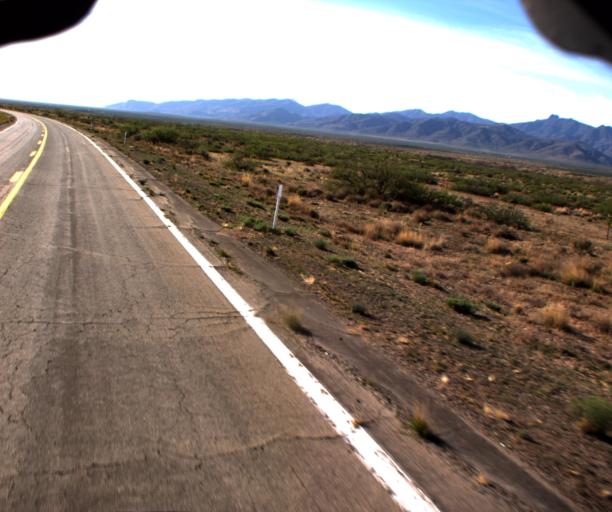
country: US
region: Arizona
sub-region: Cochise County
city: Willcox
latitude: 32.3752
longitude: -109.6420
